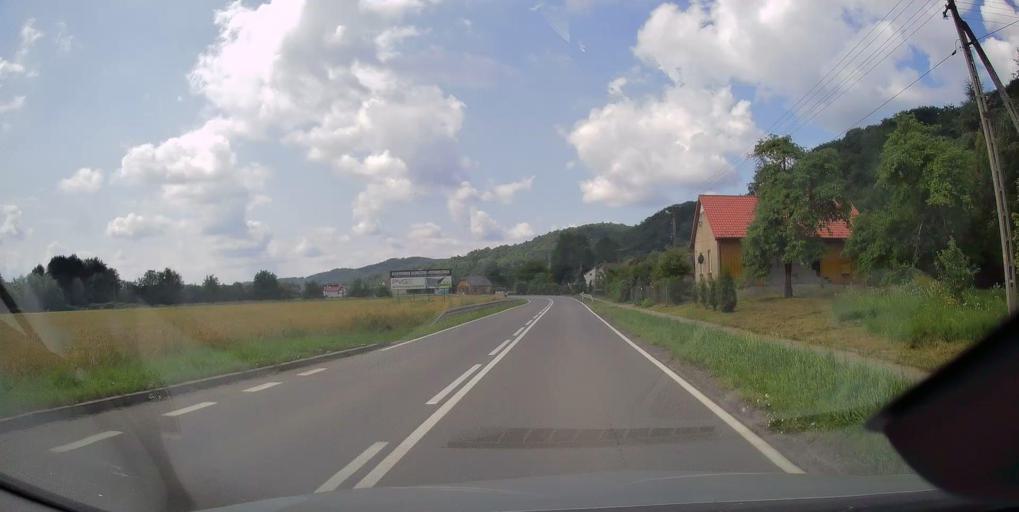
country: PL
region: Lesser Poland Voivodeship
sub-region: Powiat tarnowski
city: Wielka Wies
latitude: 49.9176
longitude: 20.8219
